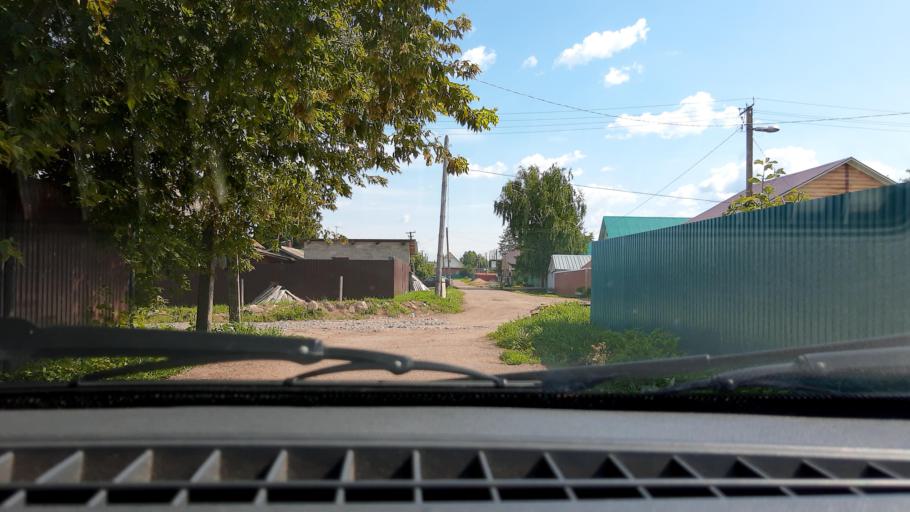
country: RU
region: Bashkortostan
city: Mikhaylovka
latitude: 54.8658
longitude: 55.8164
